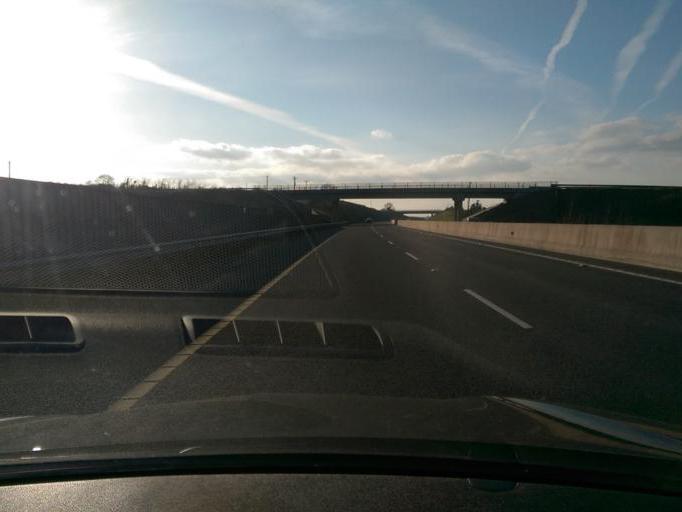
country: IE
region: Leinster
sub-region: Laois
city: Rathdowney
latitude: 52.9118
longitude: -7.5240
